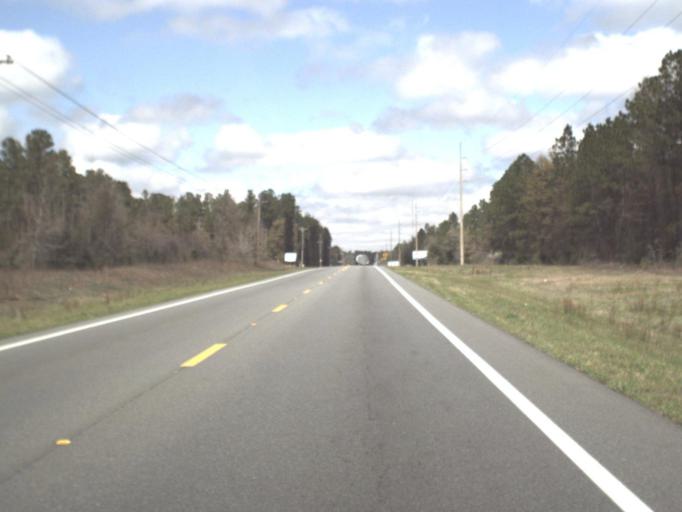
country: US
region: Florida
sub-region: Wakulla County
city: Crawfordville
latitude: 30.2572
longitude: -84.3622
